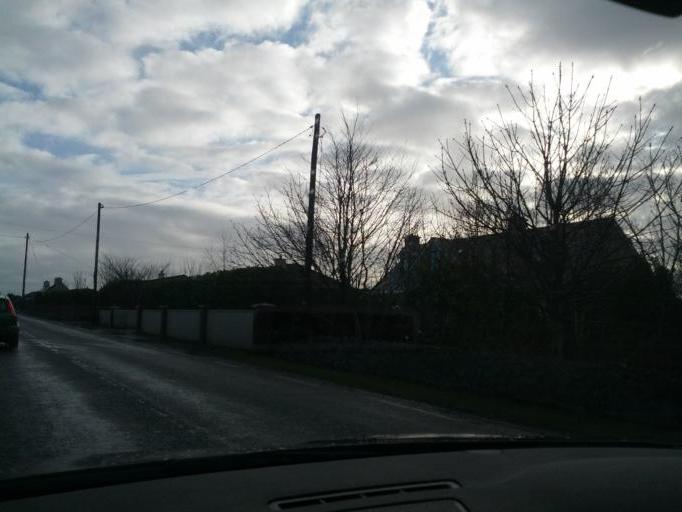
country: IE
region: Connaught
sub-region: County Galway
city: Oranmore
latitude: 53.3182
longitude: -8.8634
